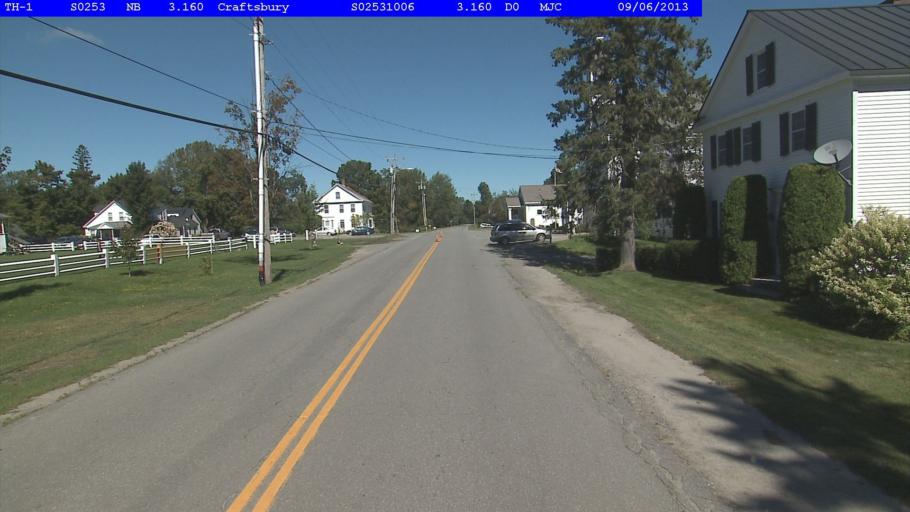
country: US
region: Vermont
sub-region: Caledonia County
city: Hardwick
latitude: 44.6536
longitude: -72.3822
